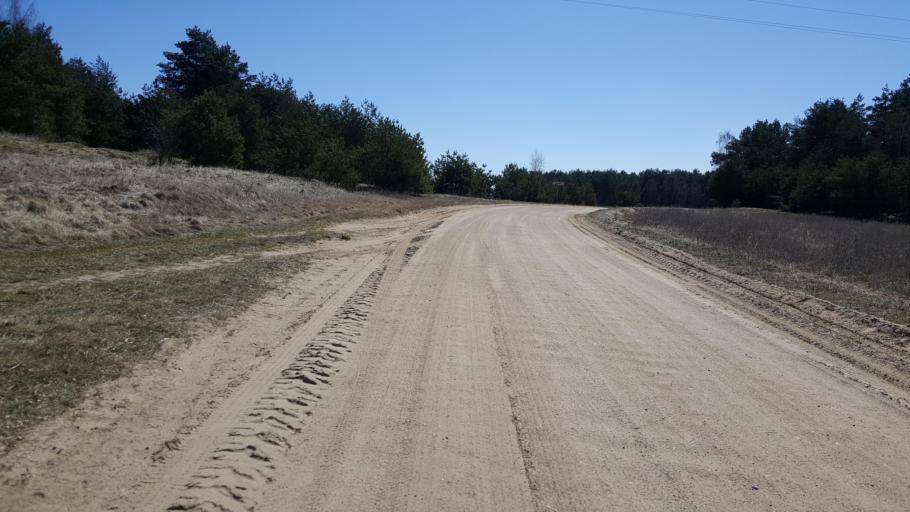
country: BY
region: Brest
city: Kamyanyets
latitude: 52.3210
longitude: 23.8649
